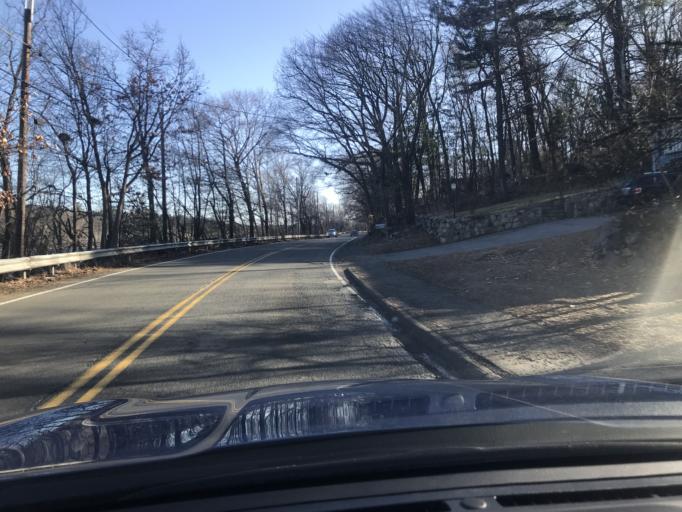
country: US
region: Massachusetts
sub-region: Essex County
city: Lynnfield
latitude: 42.5061
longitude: -71.0244
